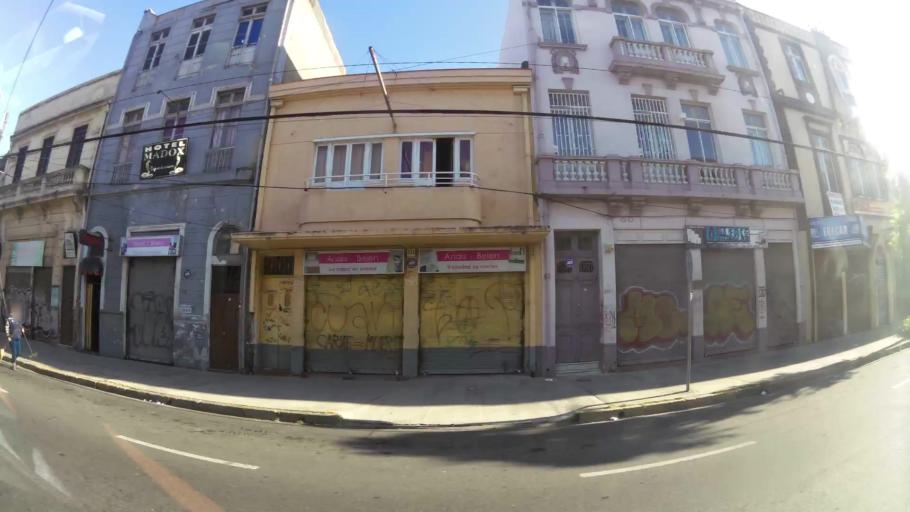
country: CL
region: Valparaiso
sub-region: Provincia de Valparaiso
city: Valparaiso
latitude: -33.0491
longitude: -71.6118
